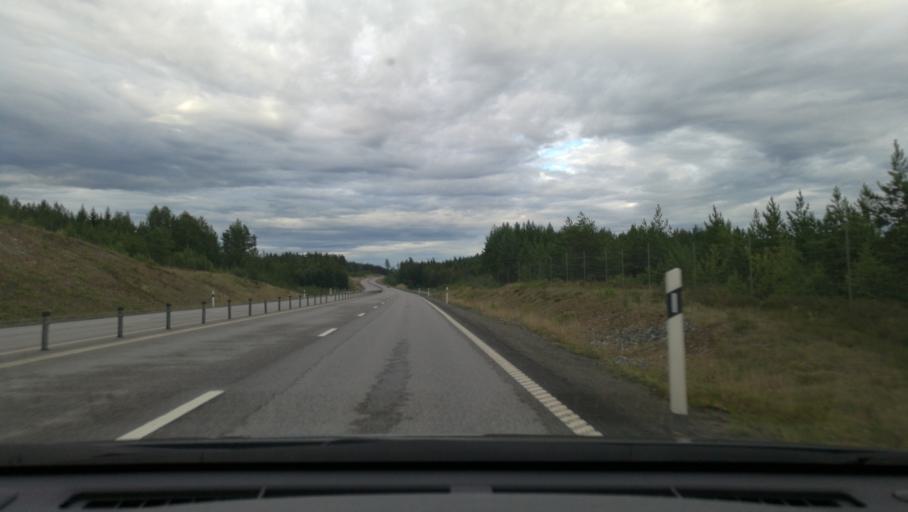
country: SE
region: OEstergoetland
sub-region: Norrkopings Kommun
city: Svartinge
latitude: 58.6694
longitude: 15.9968
